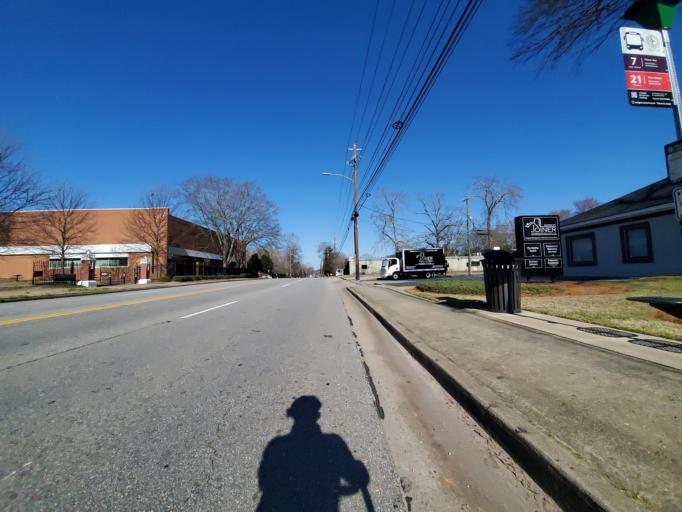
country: US
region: Georgia
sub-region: Clarke County
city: Athens
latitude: 33.9647
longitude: -83.4028
